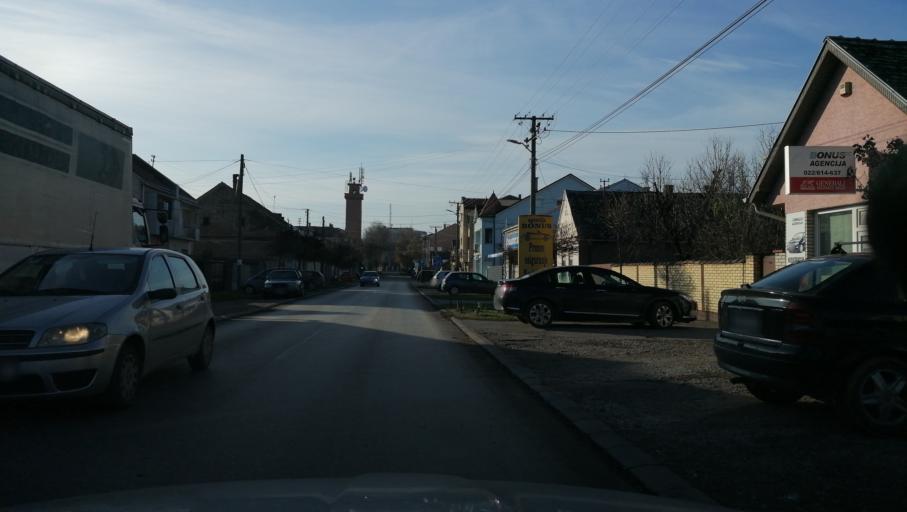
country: RS
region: Autonomna Pokrajina Vojvodina
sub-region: Sremski Okrug
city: Sremska Mitrovica
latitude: 44.9672
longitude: 19.6141
